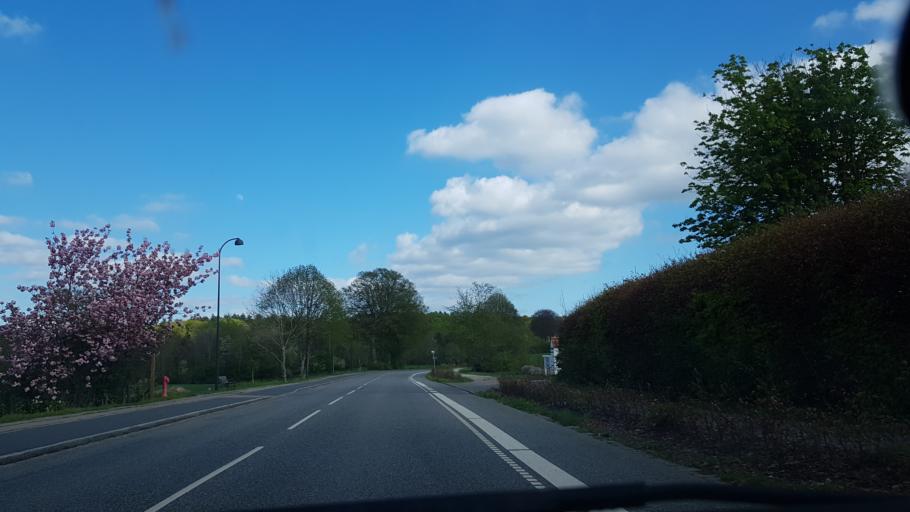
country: DK
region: Capital Region
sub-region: Rudersdal Kommune
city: Trorod
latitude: 55.8280
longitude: 12.5366
